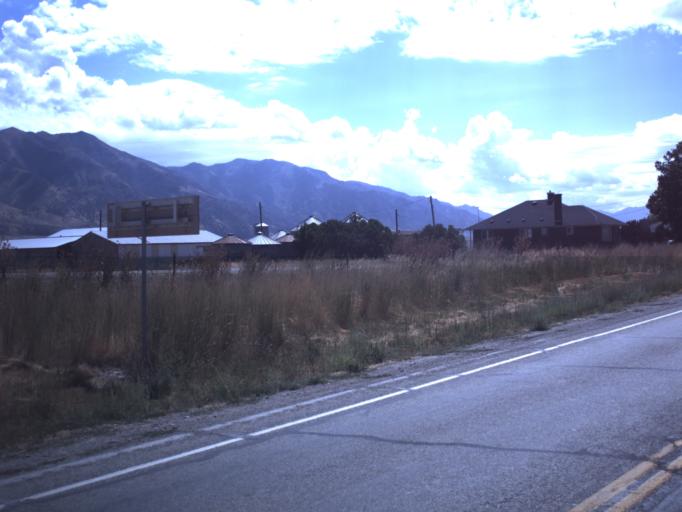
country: US
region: Utah
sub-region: Box Elder County
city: Garland
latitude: 41.7385
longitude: -112.1436
